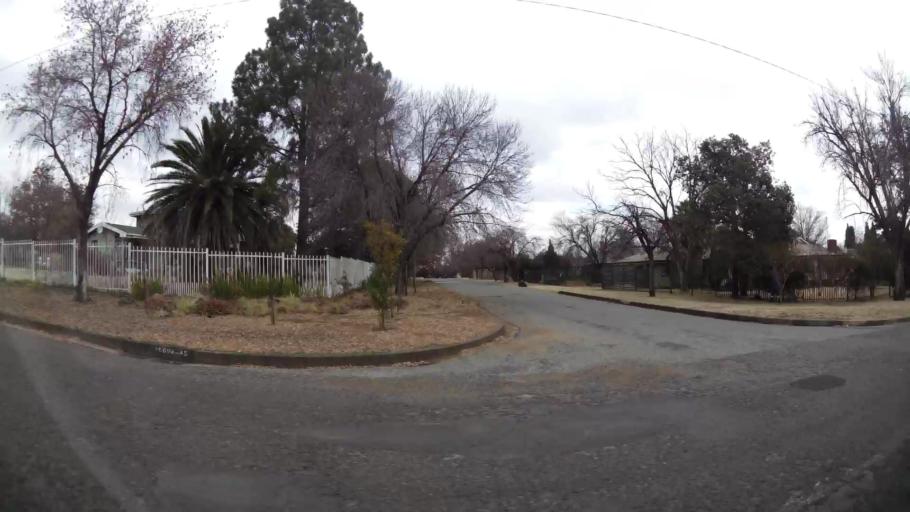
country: ZA
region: Orange Free State
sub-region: Fezile Dabi District Municipality
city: Kroonstad
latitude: -27.6855
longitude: 27.2357
